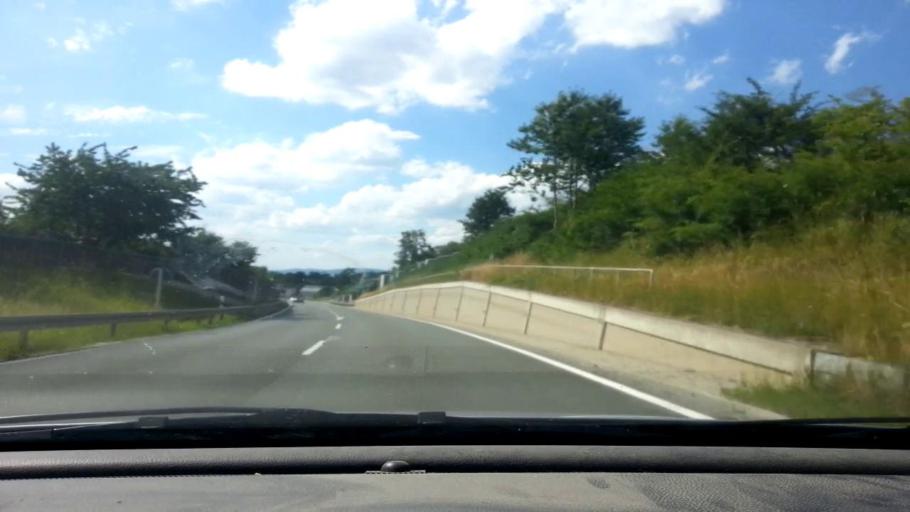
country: DE
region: Bavaria
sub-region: Upper Palatinate
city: Kastl
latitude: 49.8662
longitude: 11.9533
